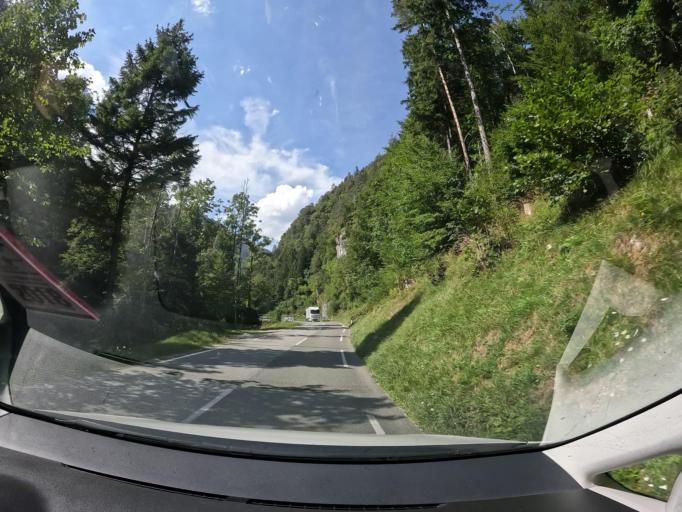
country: SI
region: Jezersko
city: Zgornje Jezersko
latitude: 46.3601
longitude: 14.4594
